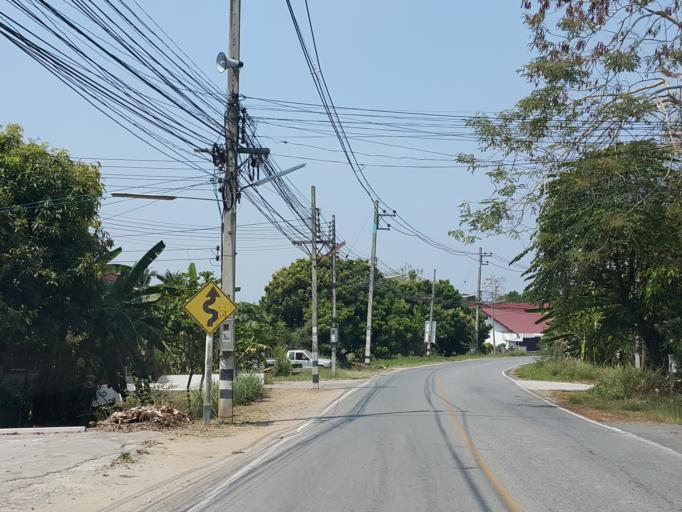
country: TH
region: Chiang Mai
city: Chiang Mai
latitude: 18.7425
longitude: 98.9901
